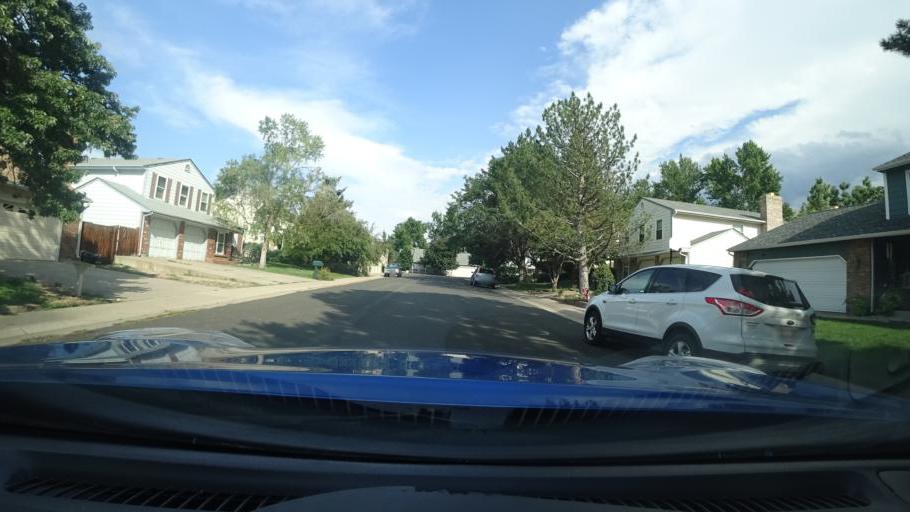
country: US
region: Colorado
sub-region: Adams County
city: Aurora
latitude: 39.6910
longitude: -104.8032
